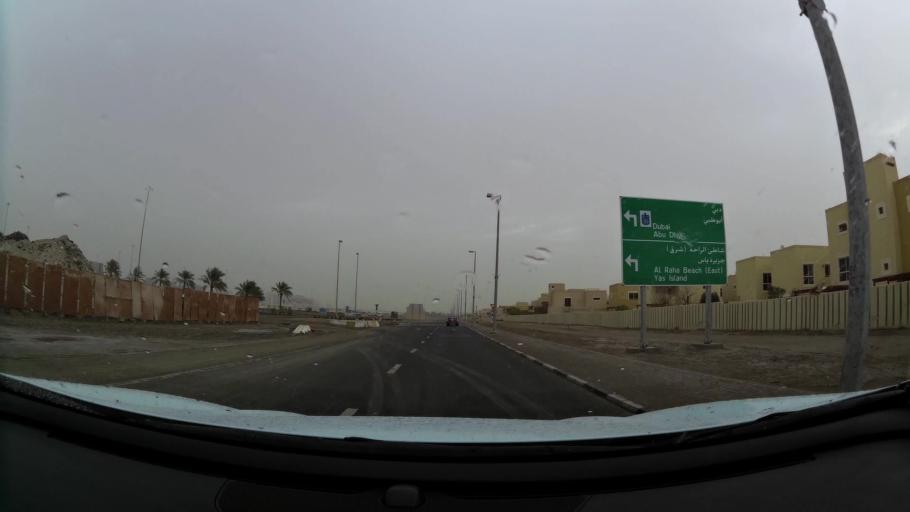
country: AE
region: Abu Dhabi
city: Abu Dhabi
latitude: 24.4406
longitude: 54.5923
